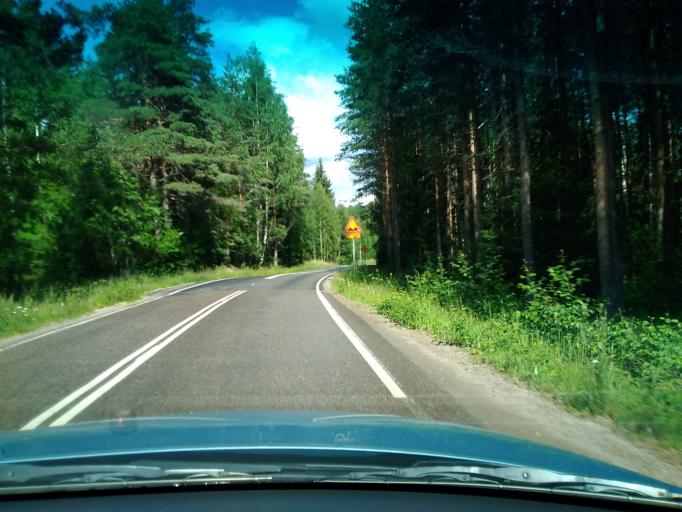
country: FI
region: Central Finland
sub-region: Saarijaervi-Viitasaari
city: Saarijaervi
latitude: 62.7339
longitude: 25.1223
